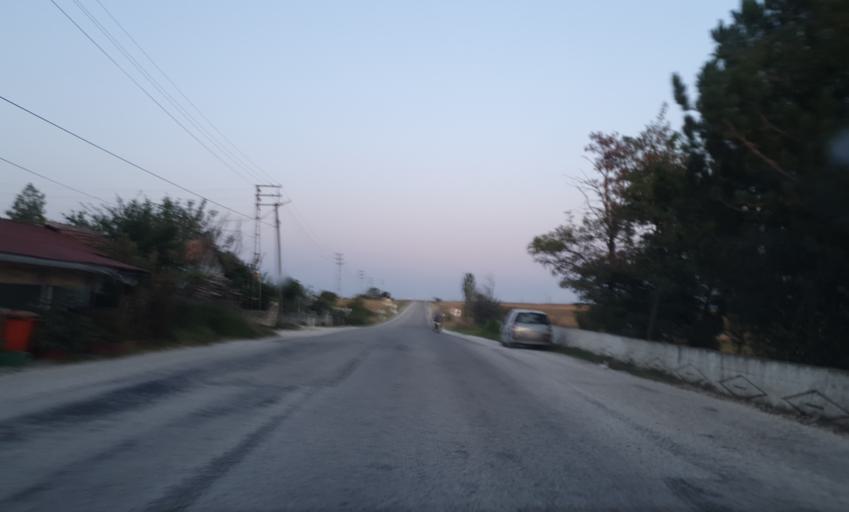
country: TR
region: Kirklareli
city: Pinarhisar
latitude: 41.6274
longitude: 27.5706
